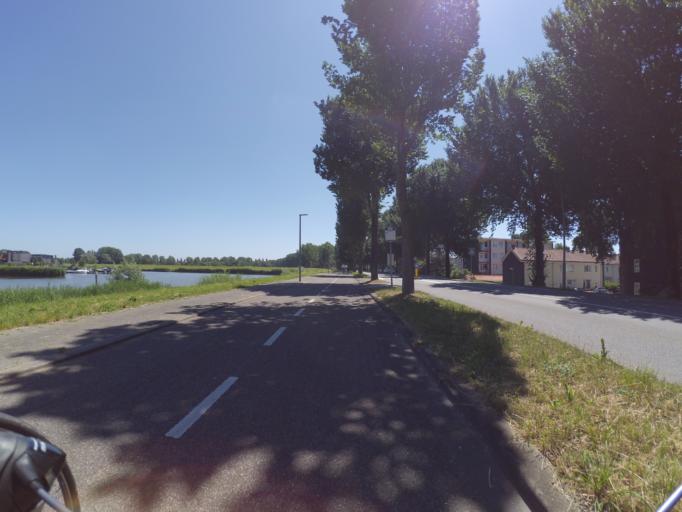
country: NL
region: South Holland
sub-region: Gemeente Dordrecht
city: Dordrecht
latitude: 51.8093
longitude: 4.6907
